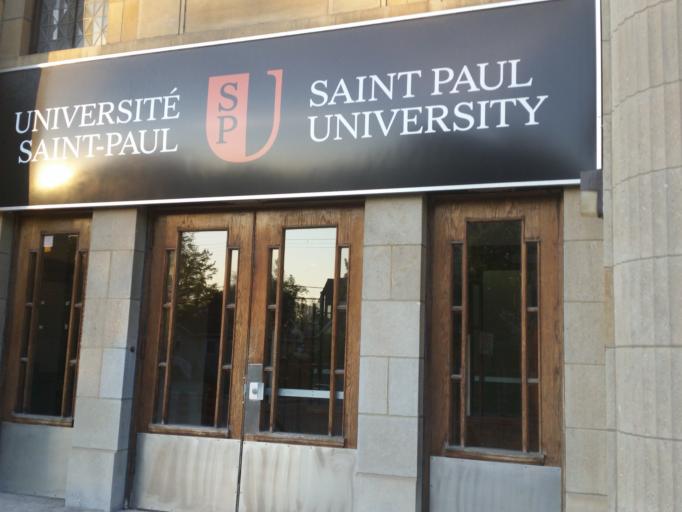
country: CA
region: Ontario
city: Ottawa
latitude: 45.4069
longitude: -75.6763
